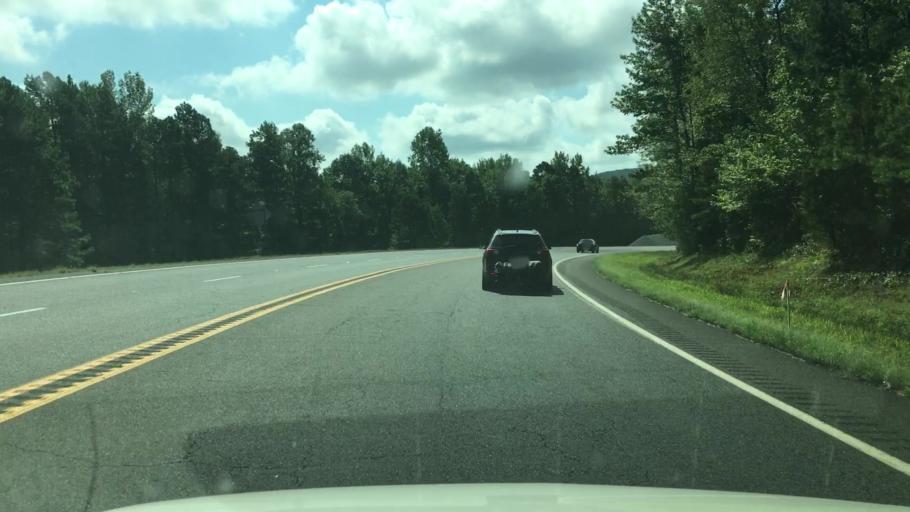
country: US
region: Arkansas
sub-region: Garland County
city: Lake Hamilton
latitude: 34.3682
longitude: -93.1630
